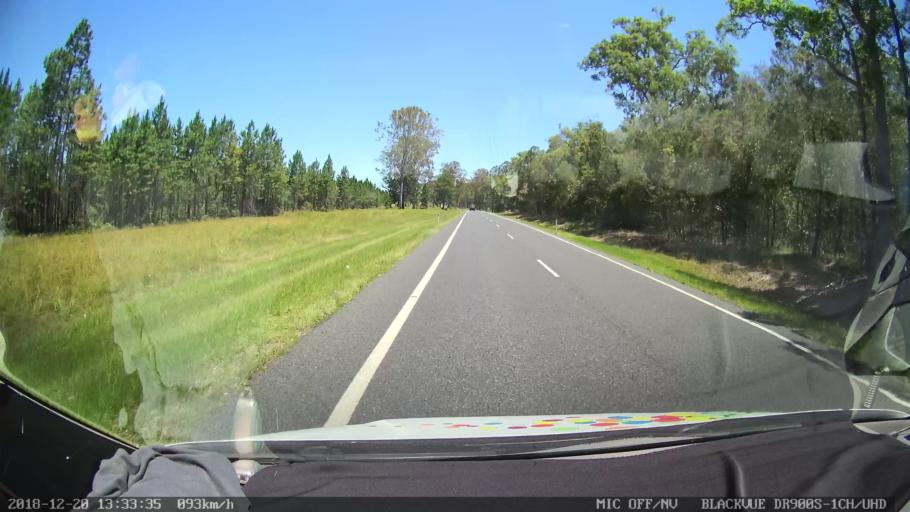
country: AU
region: New South Wales
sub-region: Clarence Valley
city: Gordon
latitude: -29.2474
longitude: 152.9860
